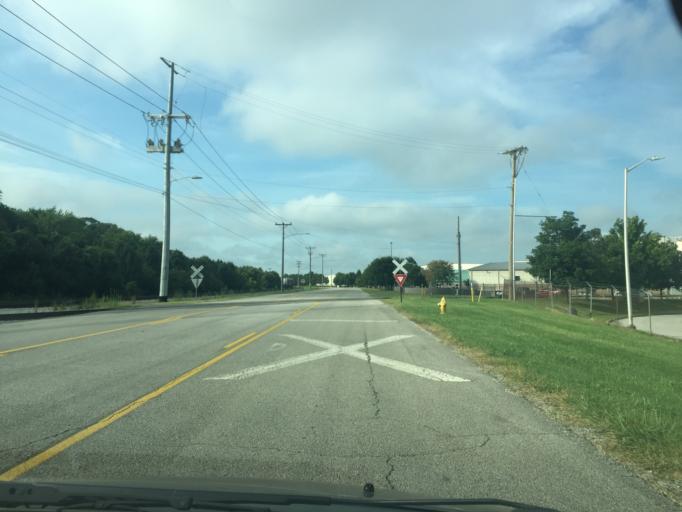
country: US
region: Tennessee
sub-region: Hamilton County
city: East Chattanooga
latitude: 35.0794
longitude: -85.2712
